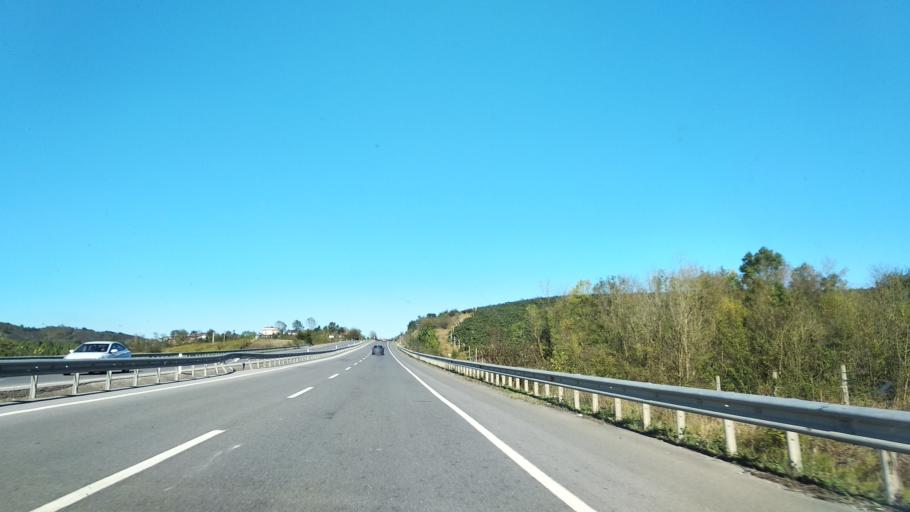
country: TR
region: Sakarya
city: Ortakoy
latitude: 41.0420
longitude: 30.6227
